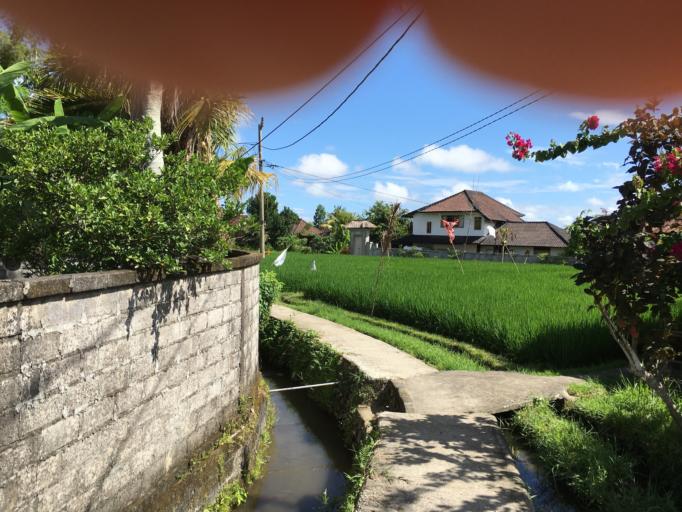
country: ID
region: Bali
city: Banjar Pande
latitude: -8.4995
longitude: 115.2513
